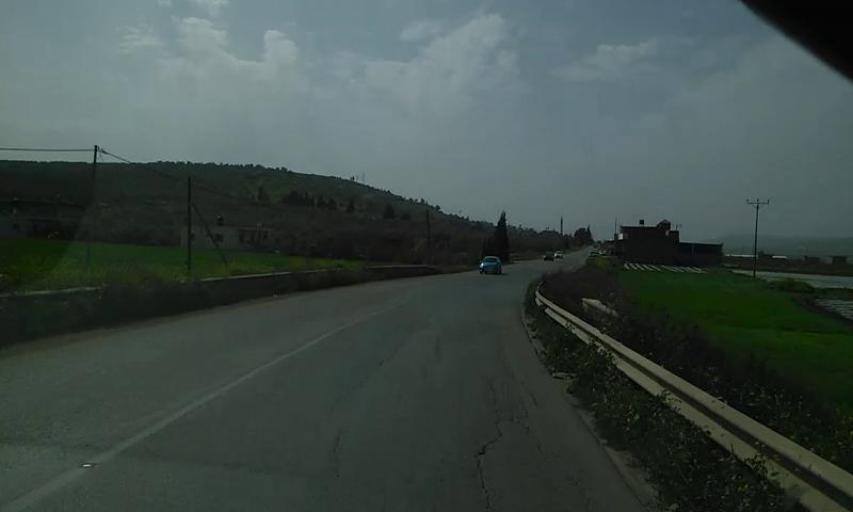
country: PS
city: Bir al Basha
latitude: 32.4247
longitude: 35.2478
